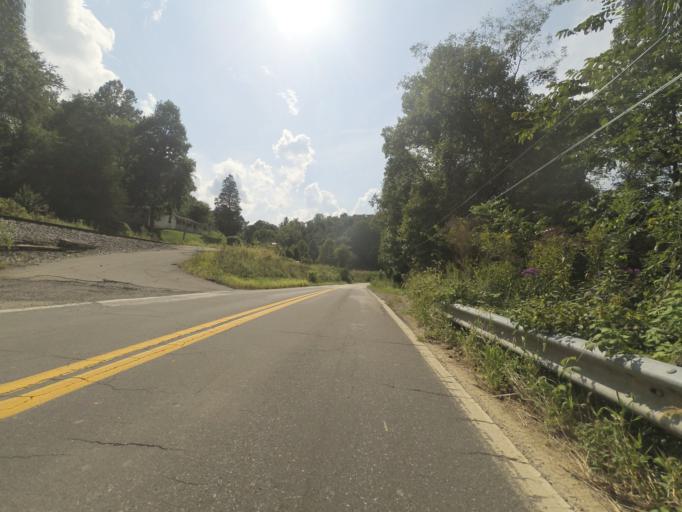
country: US
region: West Virginia
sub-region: Wayne County
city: Ceredo
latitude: 38.3716
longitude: -82.5491
